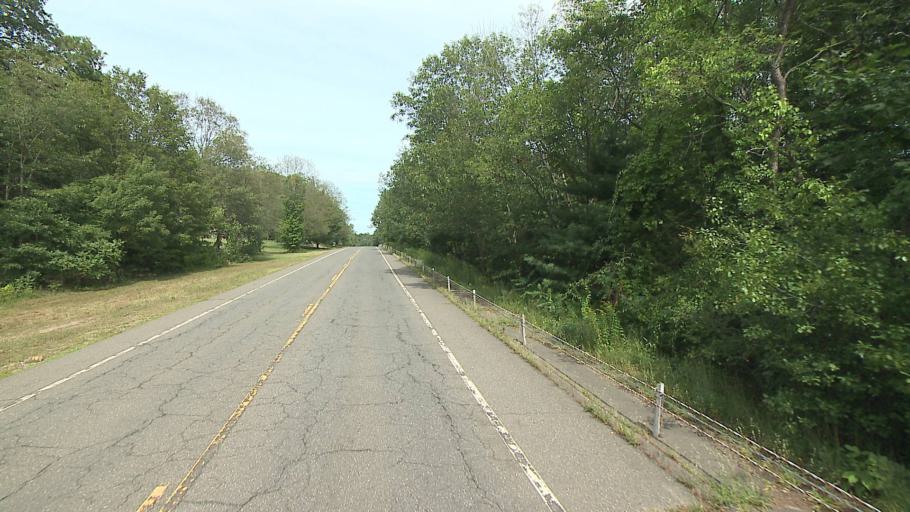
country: US
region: Connecticut
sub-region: Litchfield County
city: Oakville
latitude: 41.6101
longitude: -73.0500
